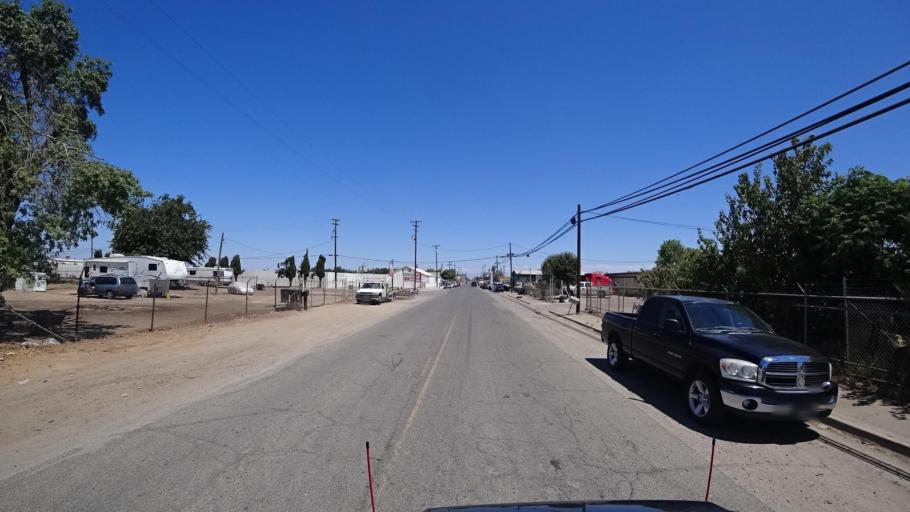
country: US
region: California
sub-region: Fresno County
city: Easton
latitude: 36.6846
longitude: -119.7457
